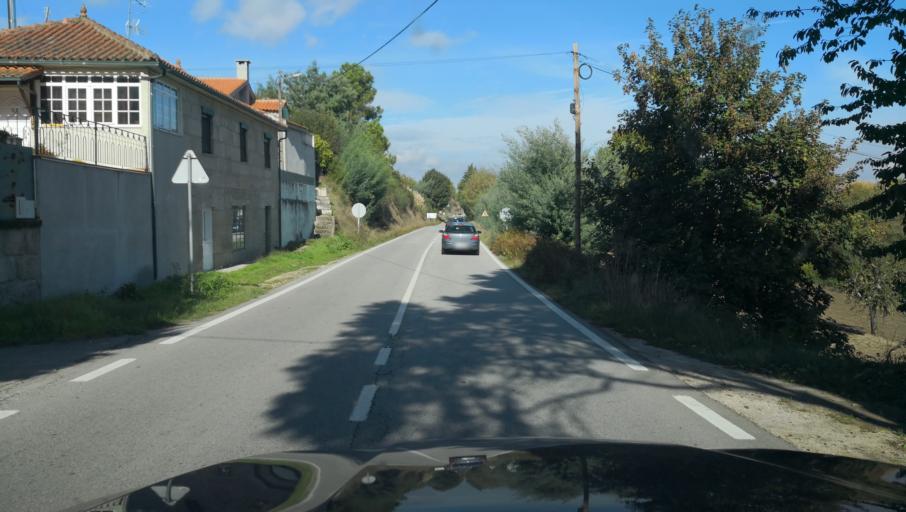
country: PT
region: Vila Real
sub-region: Chaves
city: Chaves
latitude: 41.7261
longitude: -7.4789
